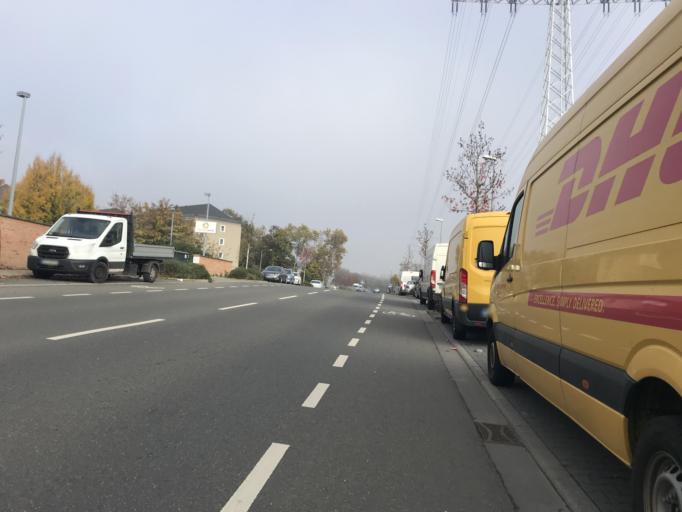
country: DE
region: Hesse
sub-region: Regierungsbezirk Darmstadt
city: Wiesbaden
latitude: 50.0387
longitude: 8.2468
